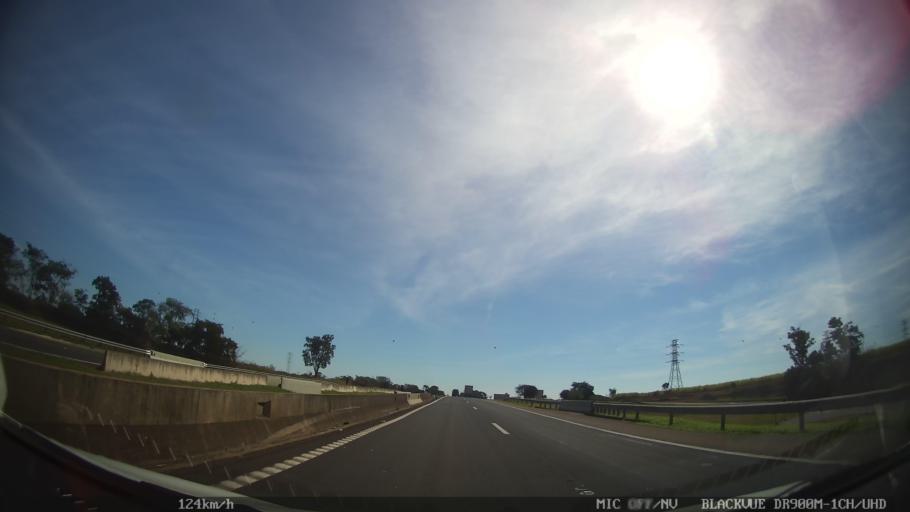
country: BR
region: Sao Paulo
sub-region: Porto Ferreira
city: Porto Ferreira
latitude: -21.9108
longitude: -47.4755
